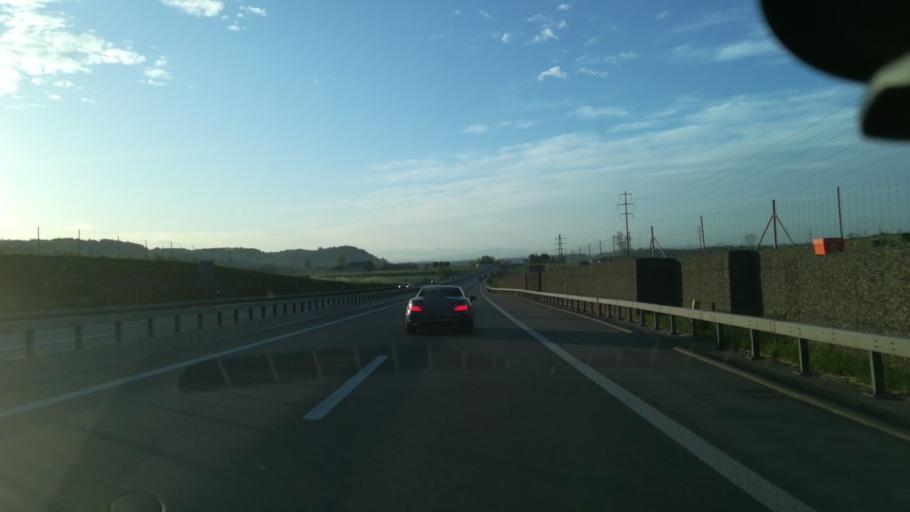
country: CH
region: Zurich
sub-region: Bezirk Andelfingen
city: Uhwiesen
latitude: 47.6569
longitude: 8.6353
